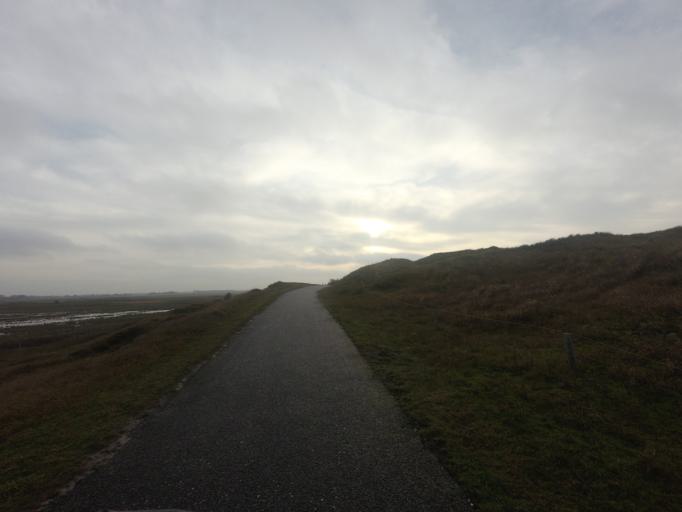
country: NL
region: North Holland
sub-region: Gemeente Texel
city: Den Burg
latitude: 53.1491
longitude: 4.8377
